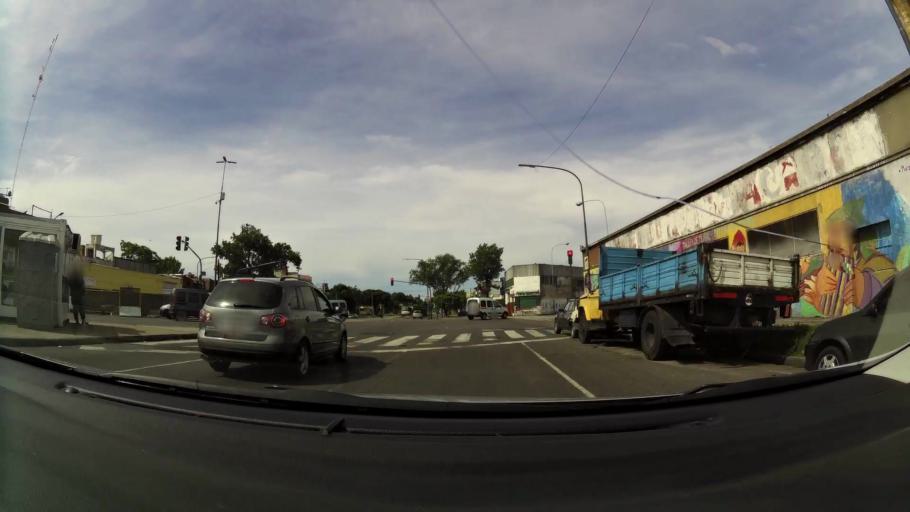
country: AR
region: Buenos Aires F.D.
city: Villa Lugano
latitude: -34.6506
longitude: -58.4312
